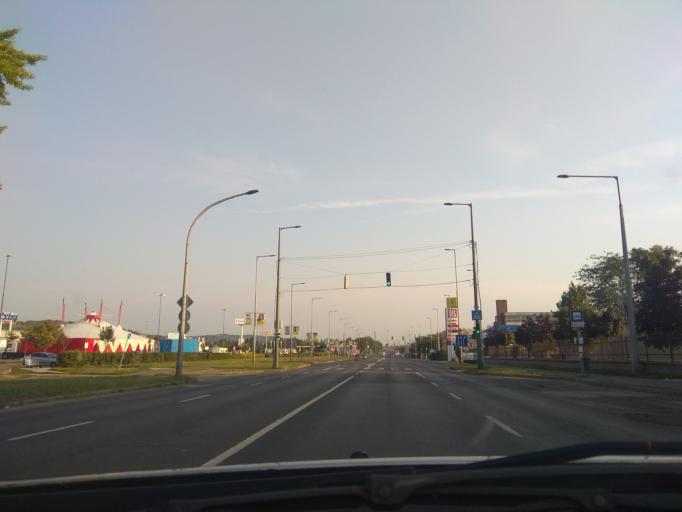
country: HU
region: Borsod-Abauj-Zemplen
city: Miskolc
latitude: 48.1256
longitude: 20.7852
